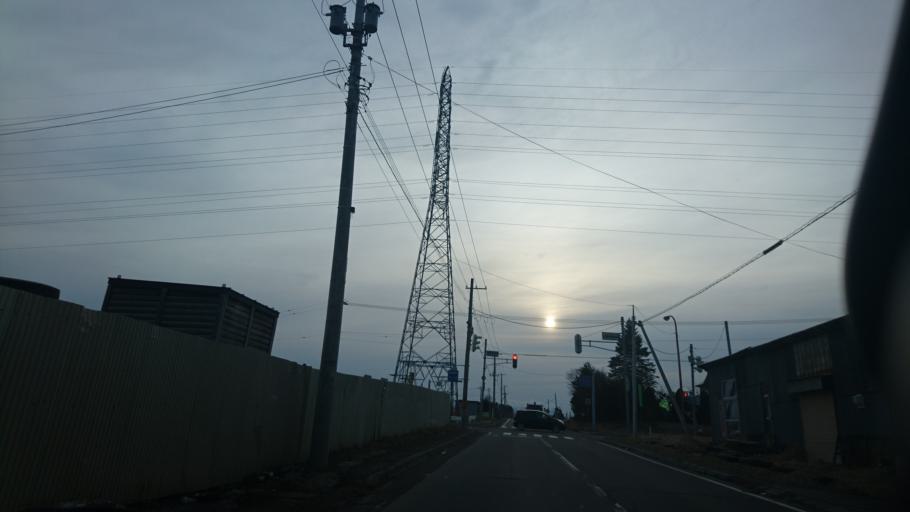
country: JP
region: Hokkaido
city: Otofuke
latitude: 42.9769
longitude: 143.1987
